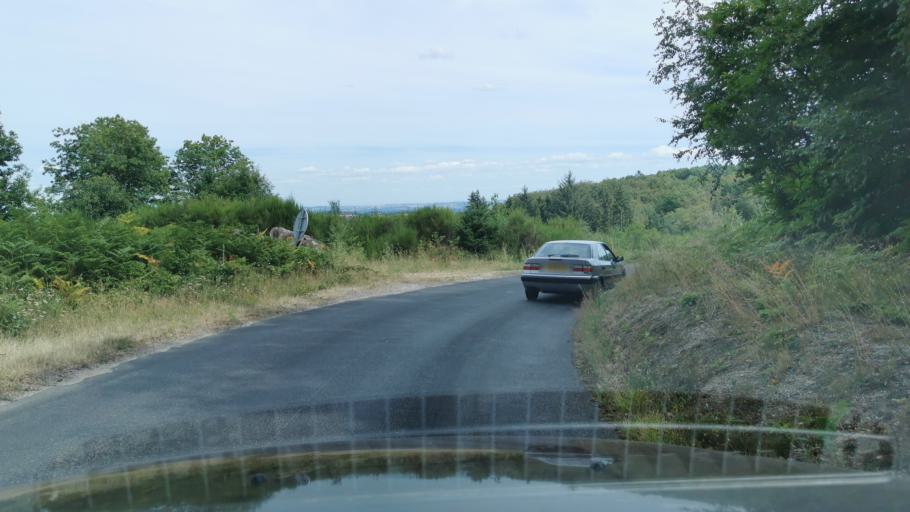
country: FR
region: Bourgogne
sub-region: Departement de Saone-et-Loire
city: Marmagne
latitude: 46.8081
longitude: 4.2878
